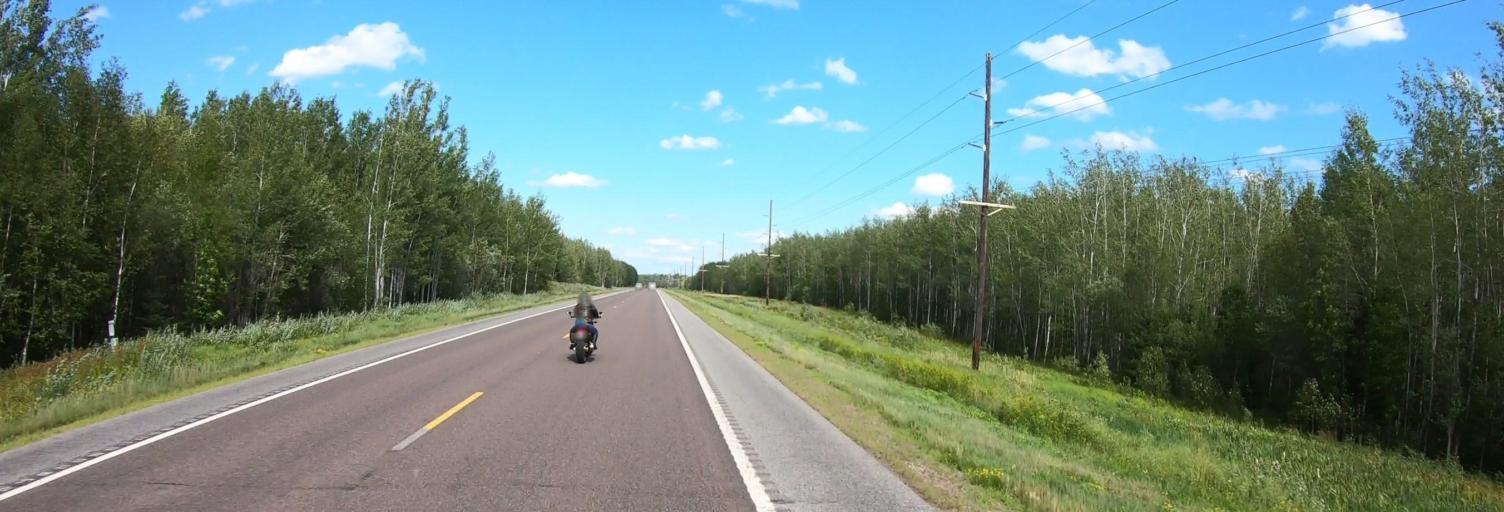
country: US
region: Minnesota
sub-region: Saint Louis County
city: Virginia
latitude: 47.8513
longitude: -92.4982
